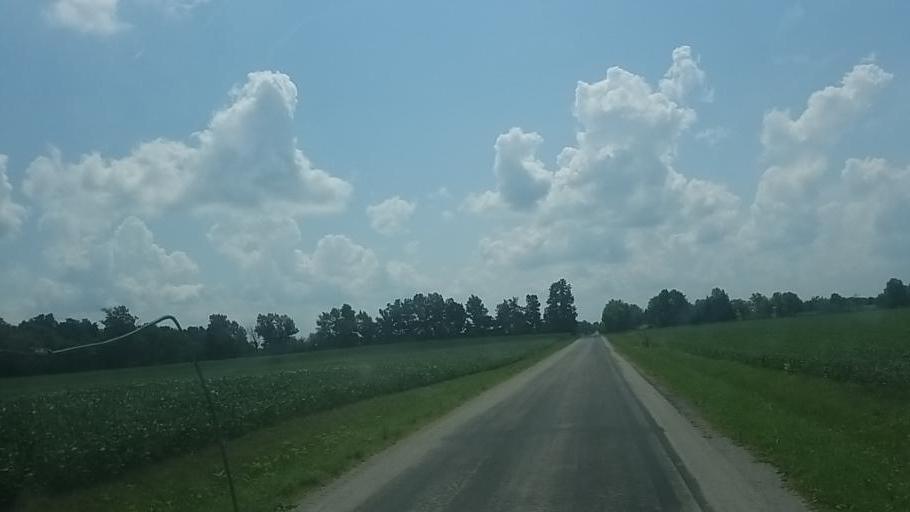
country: US
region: Ohio
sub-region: Marion County
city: Marion
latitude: 40.7332
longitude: -83.1499
